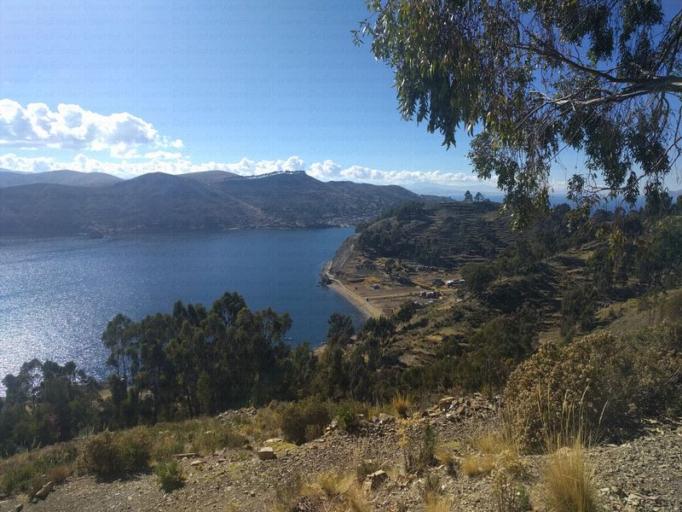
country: BO
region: La Paz
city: San Pedro
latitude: -16.2165
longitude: -68.8672
